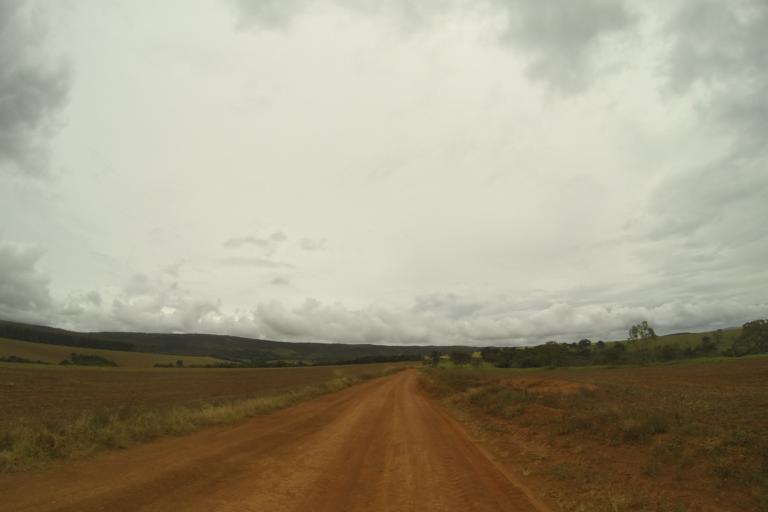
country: BR
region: Minas Gerais
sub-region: Ibia
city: Ibia
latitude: -19.7428
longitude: -46.6149
